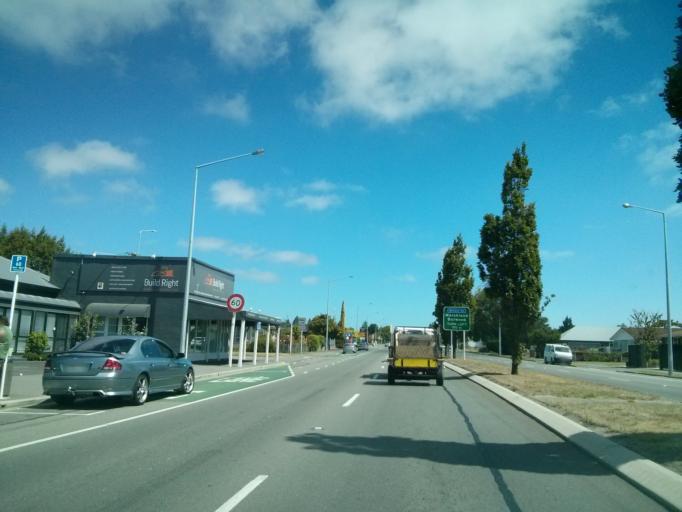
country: NZ
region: Canterbury
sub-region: Waimakariri District
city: Kaiapoi
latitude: -43.4474
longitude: 172.6309
